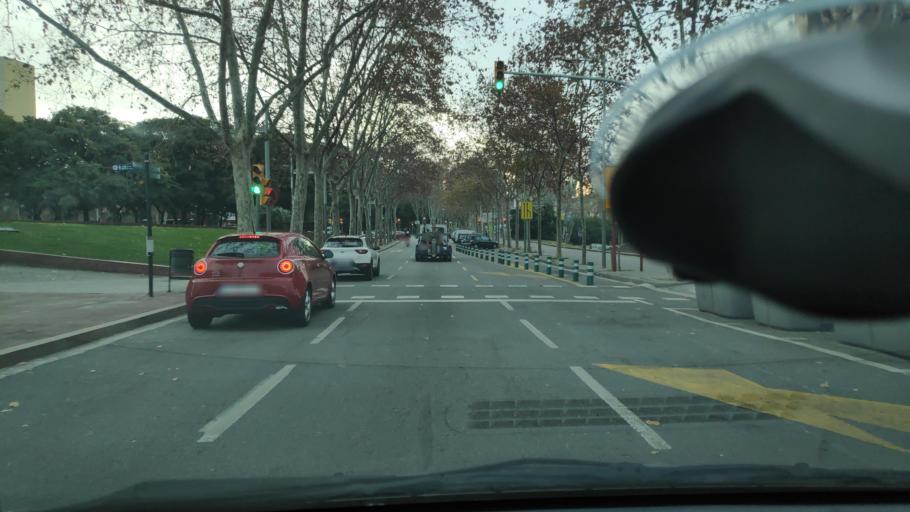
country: ES
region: Catalonia
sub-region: Provincia de Barcelona
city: Sant Marti
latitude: 41.4191
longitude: 2.2084
